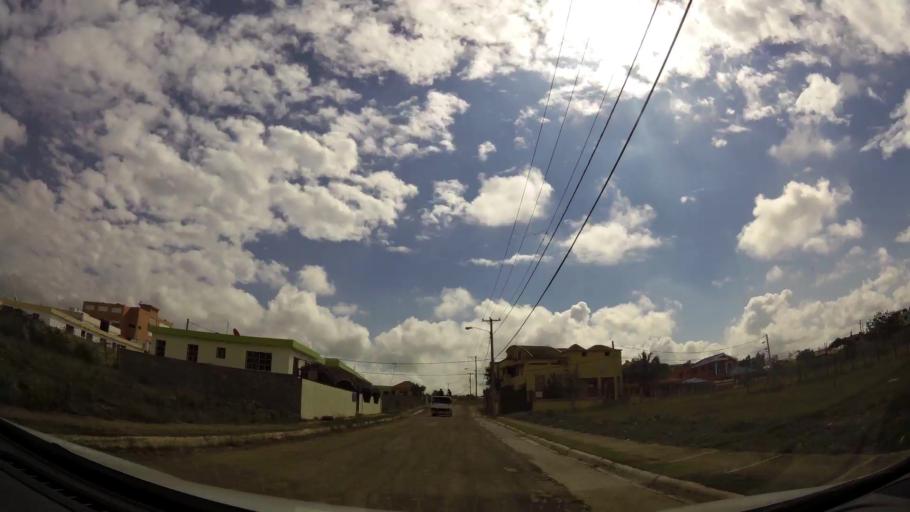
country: DO
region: Santiago
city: Palmar Arriba
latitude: 19.4900
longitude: -70.7300
